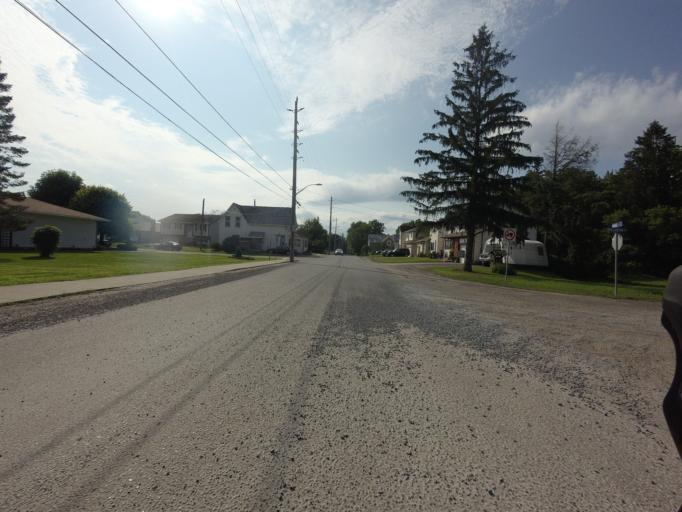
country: CA
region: Ontario
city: Prescott
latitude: 45.0203
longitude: -75.6378
